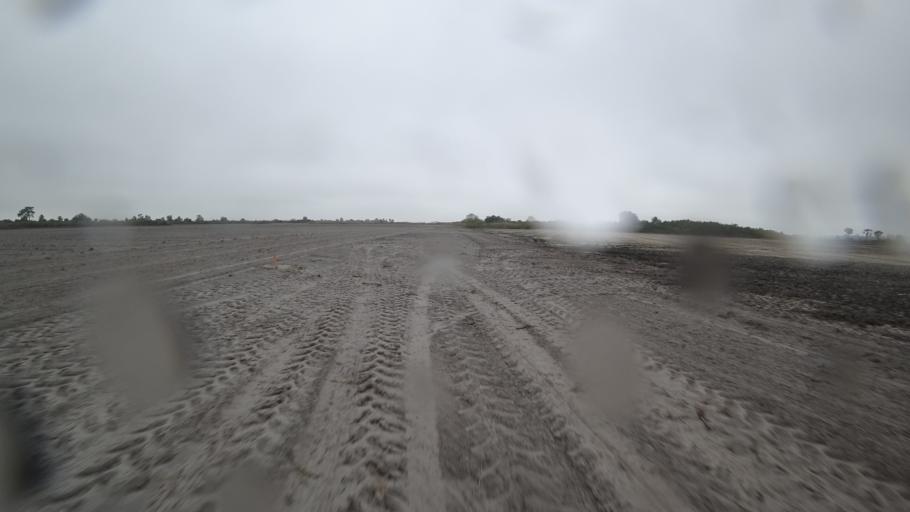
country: US
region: Florida
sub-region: Sarasota County
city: Warm Mineral Springs
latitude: 27.2989
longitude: -82.1672
